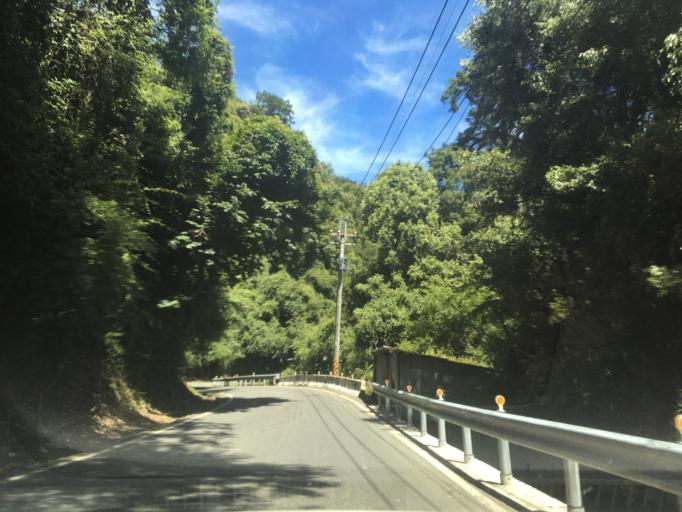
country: TW
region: Taiwan
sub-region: Nantou
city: Puli
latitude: 24.2268
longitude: 121.2559
